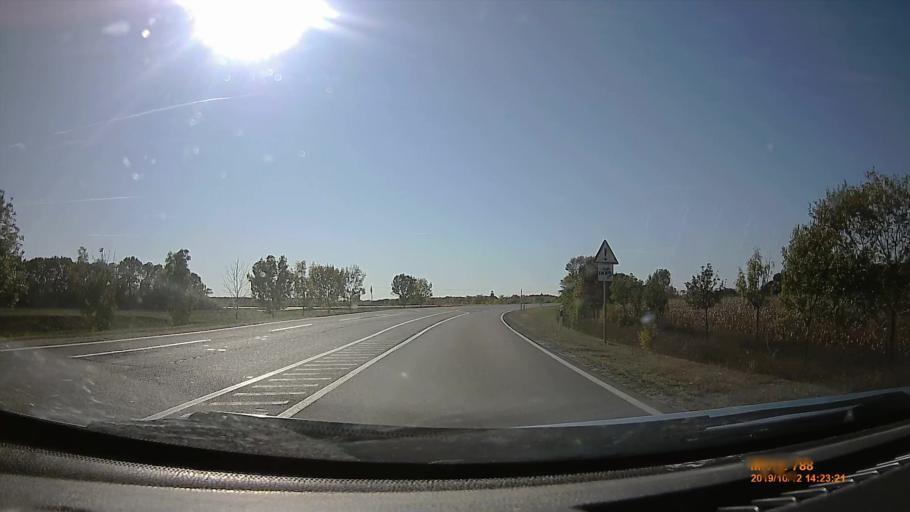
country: HU
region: Hajdu-Bihar
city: Biharkeresztes
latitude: 47.1360
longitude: 21.7016
